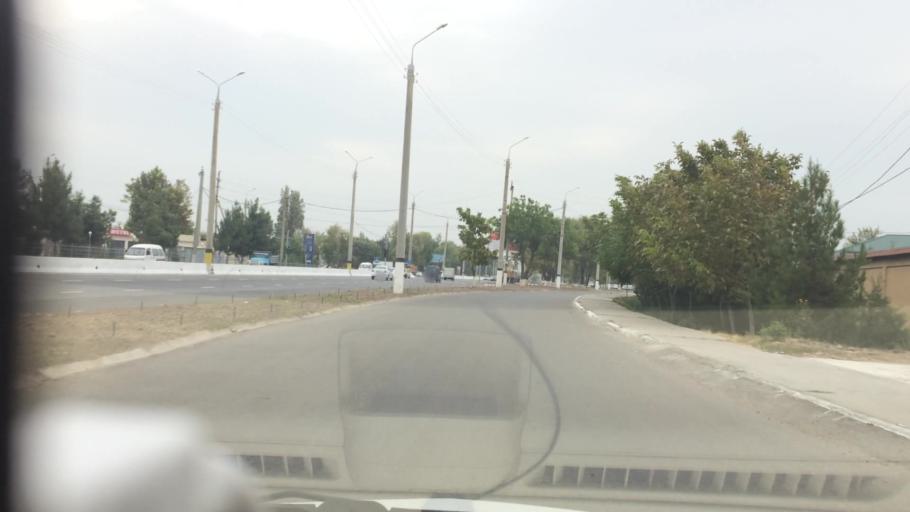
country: UZ
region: Toshkent
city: Salor
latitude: 41.3099
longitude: 69.3445
